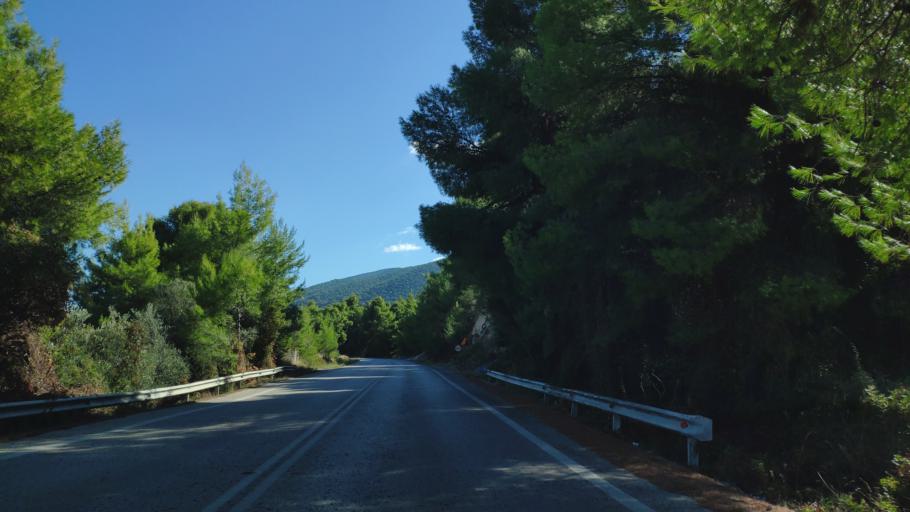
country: GR
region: Peloponnese
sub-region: Nomos Korinthias
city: Loutra Oraias Elenis
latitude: 37.8344
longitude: 23.0216
